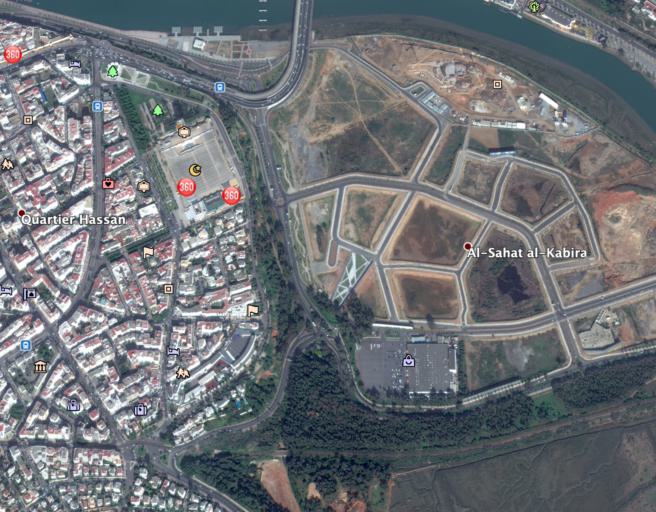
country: MA
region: Rabat-Sale-Zemmour-Zaer
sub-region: Rabat
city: Rabat
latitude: 34.0258
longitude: -6.8156
